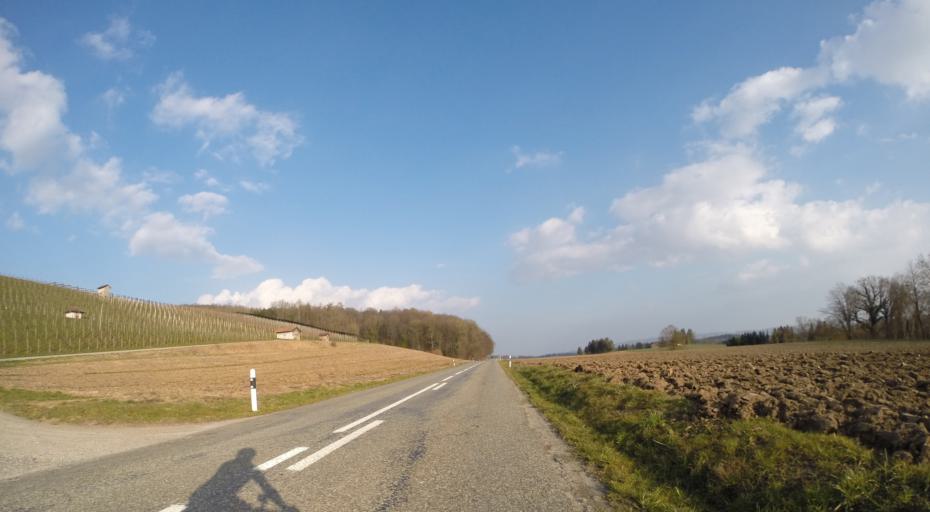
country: CH
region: Thurgau
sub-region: Frauenfeld District
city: Huttwilen
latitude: 47.6042
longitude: 8.8775
